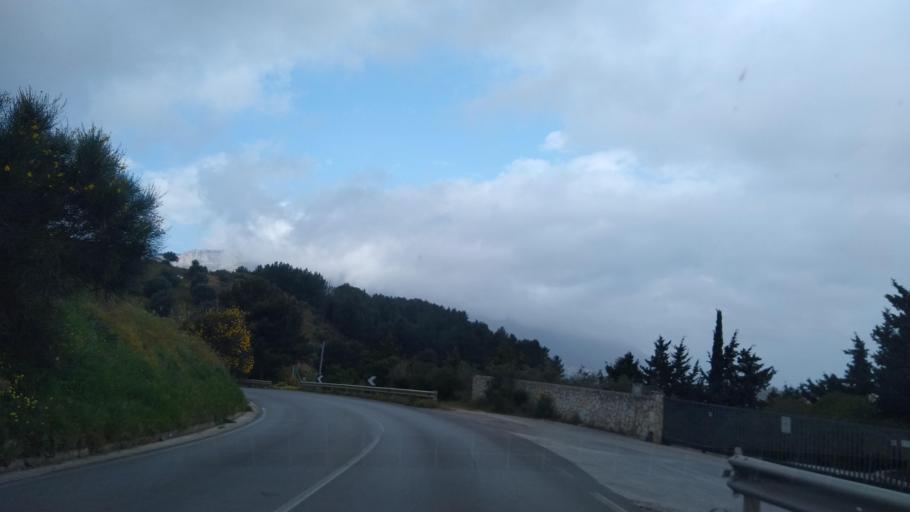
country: IT
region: Sicily
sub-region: Trapani
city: Alcamo
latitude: 37.9766
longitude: 12.9411
